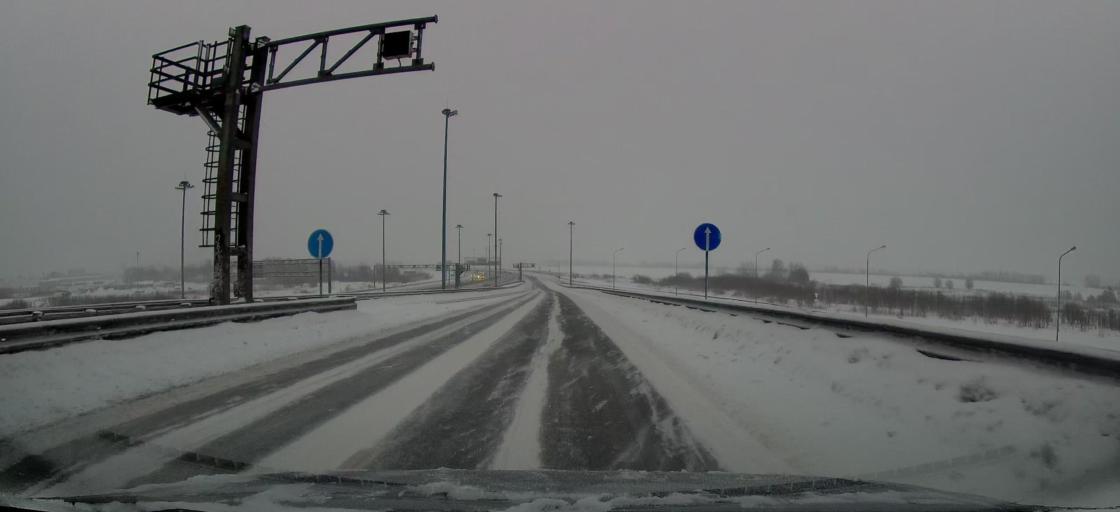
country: RU
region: St.-Petersburg
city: Uritsk
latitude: 59.7996
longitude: 30.1660
